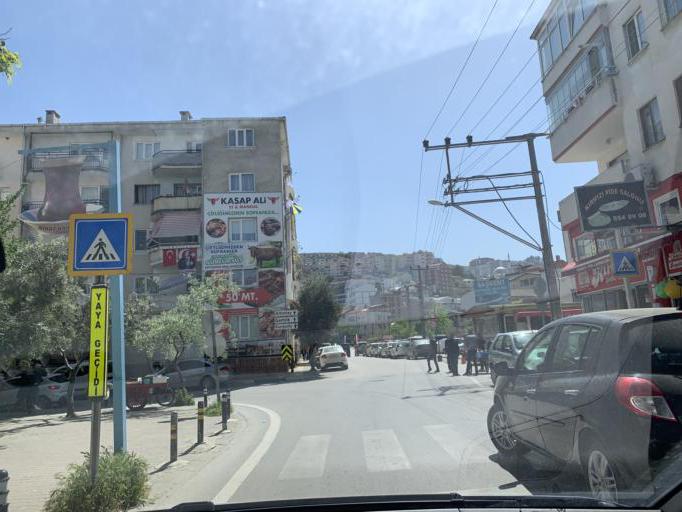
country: TR
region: Bursa
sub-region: Mudanya
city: Mudanya
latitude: 40.3544
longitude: 28.9284
